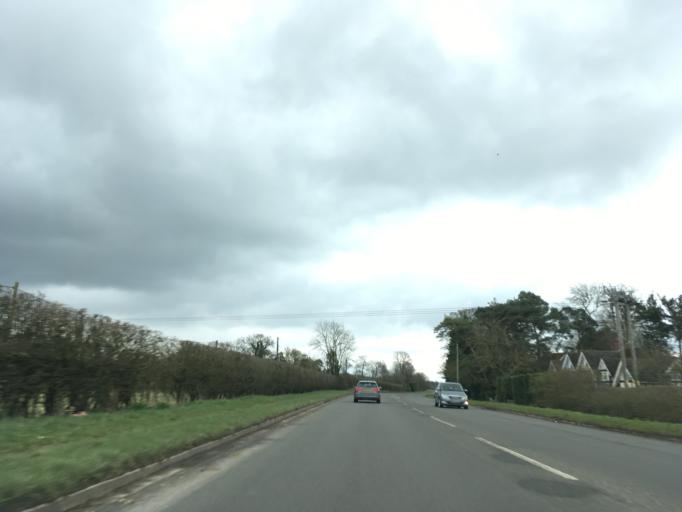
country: GB
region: England
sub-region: West Berkshire
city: Wickham
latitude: 51.4129
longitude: -1.4111
